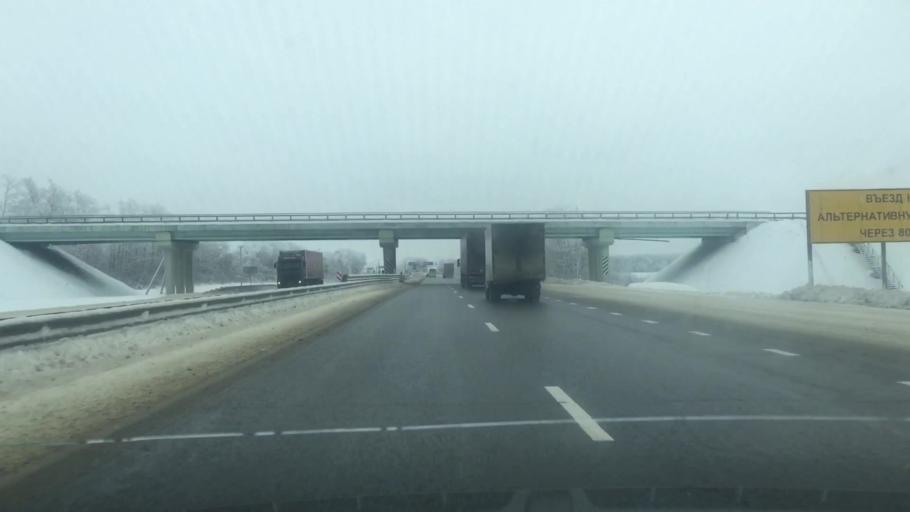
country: RU
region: Tula
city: Kazachka
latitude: 53.3000
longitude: 38.1782
